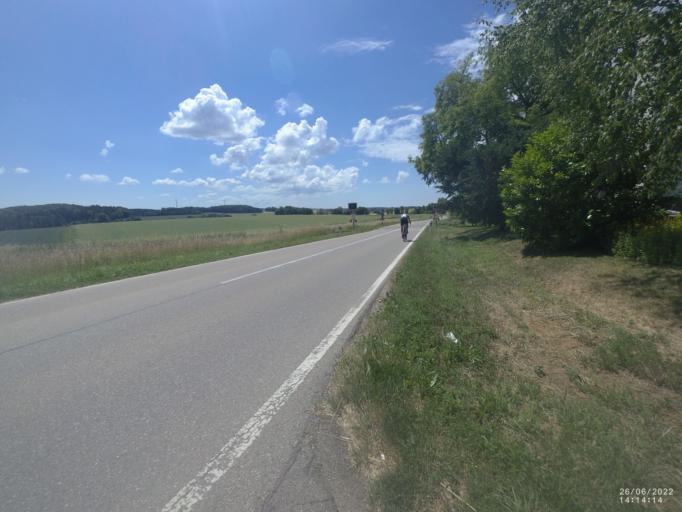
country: DE
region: Baden-Wuerttemberg
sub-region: Regierungsbezirk Stuttgart
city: Bohmenkirch
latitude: 48.6452
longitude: 9.9483
